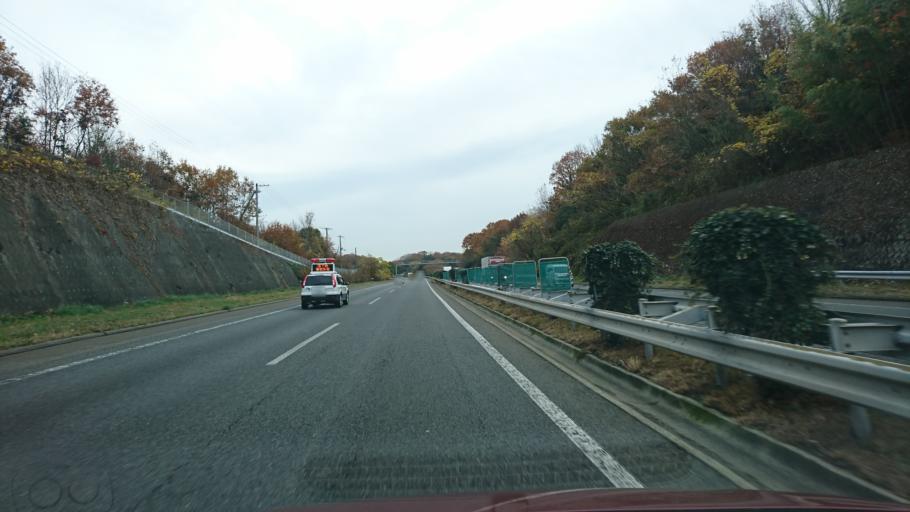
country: JP
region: Hyogo
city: Miki
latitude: 34.8212
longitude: 135.1098
